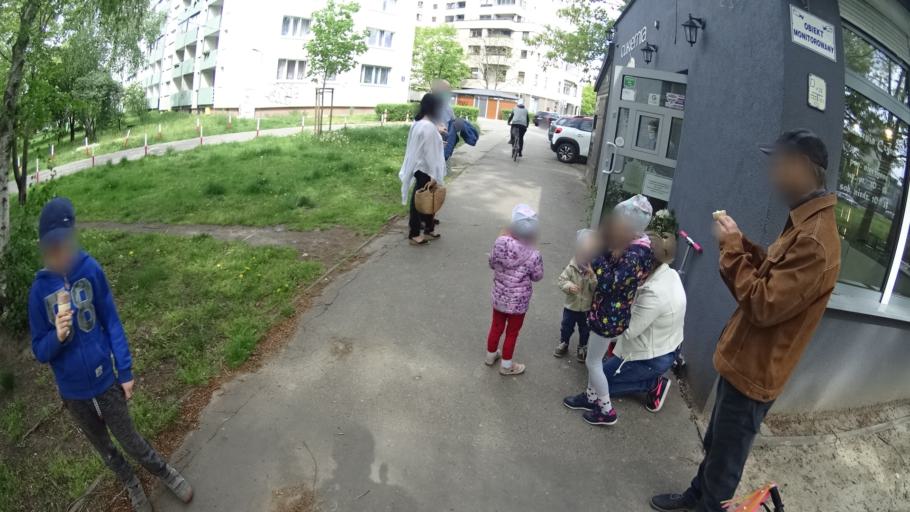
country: PL
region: Masovian Voivodeship
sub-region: Warszawa
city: Mokotow
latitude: 52.1799
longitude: 21.0121
